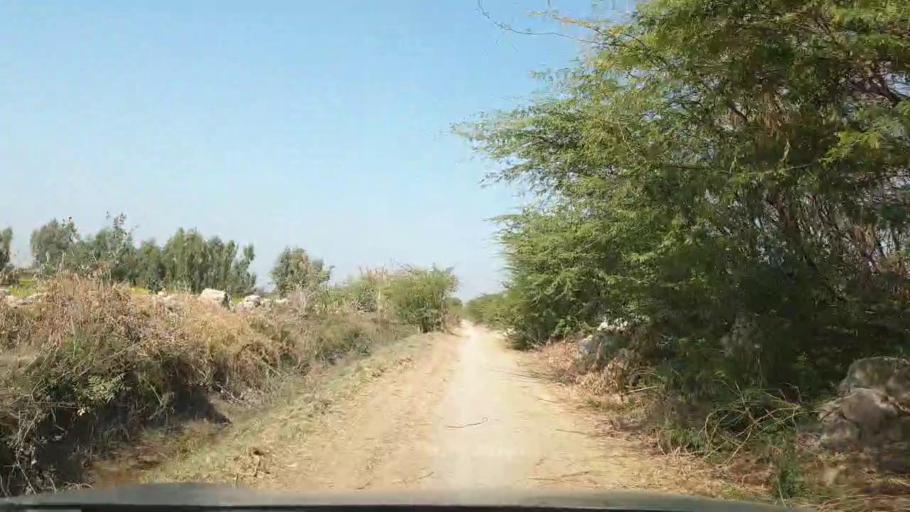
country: PK
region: Sindh
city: Berani
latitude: 25.6839
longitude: 68.8948
